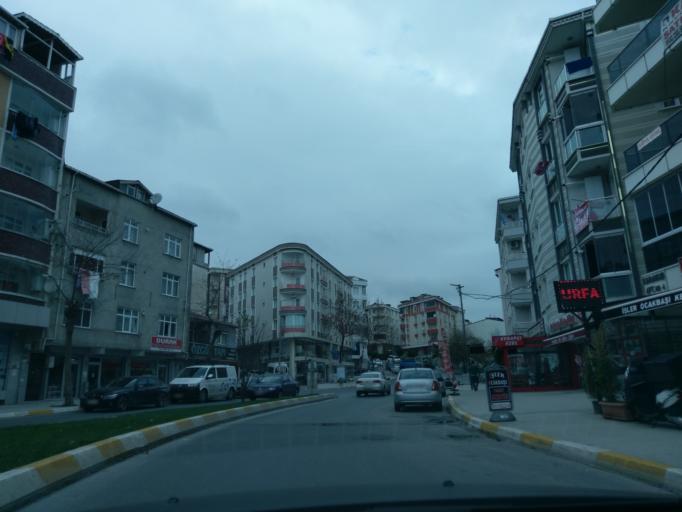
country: TR
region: Istanbul
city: Esenyurt
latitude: 41.0129
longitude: 28.6671
